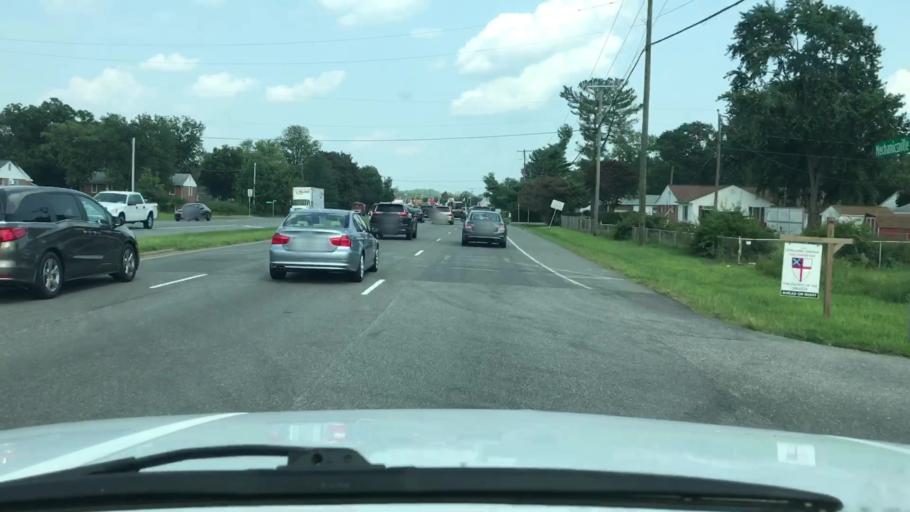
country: US
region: Virginia
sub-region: Hanover County
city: Mechanicsville
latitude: 37.6109
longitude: -77.3497
